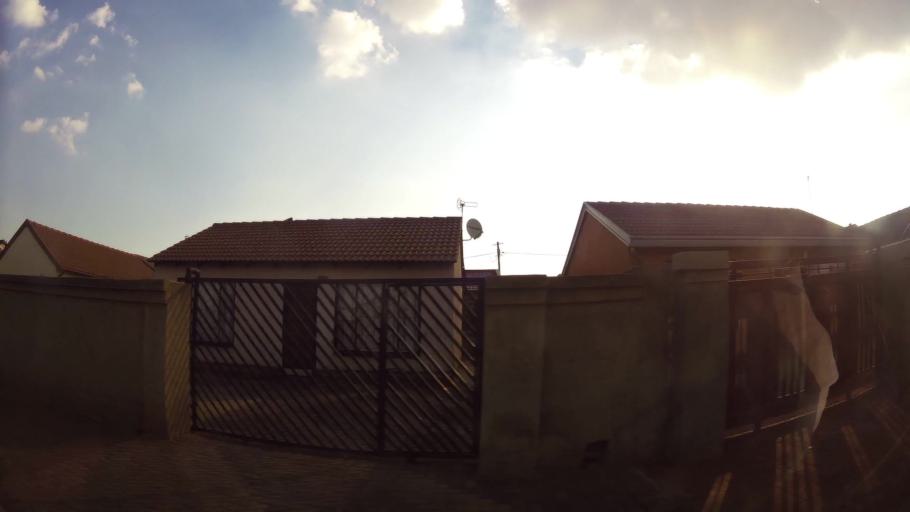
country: ZA
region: Gauteng
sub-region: Ekurhuleni Metropolitan Municipality
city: Germiston
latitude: -26.3714
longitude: 28.2266
